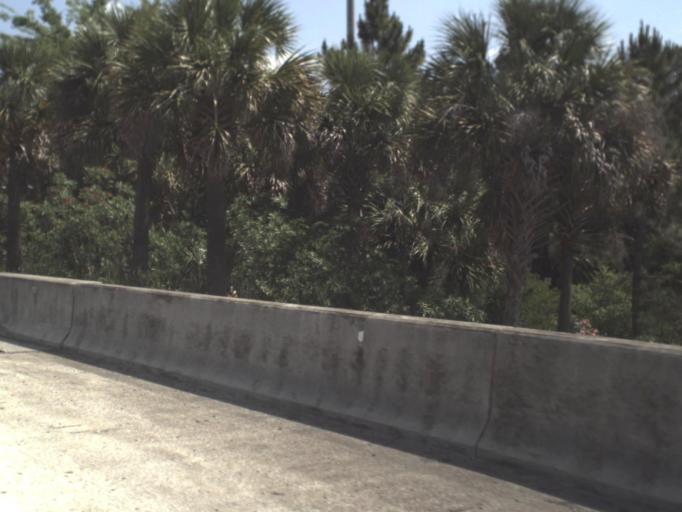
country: US
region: Florida
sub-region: Nassau County
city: Yulee
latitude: 30.5177
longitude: -81.6349
